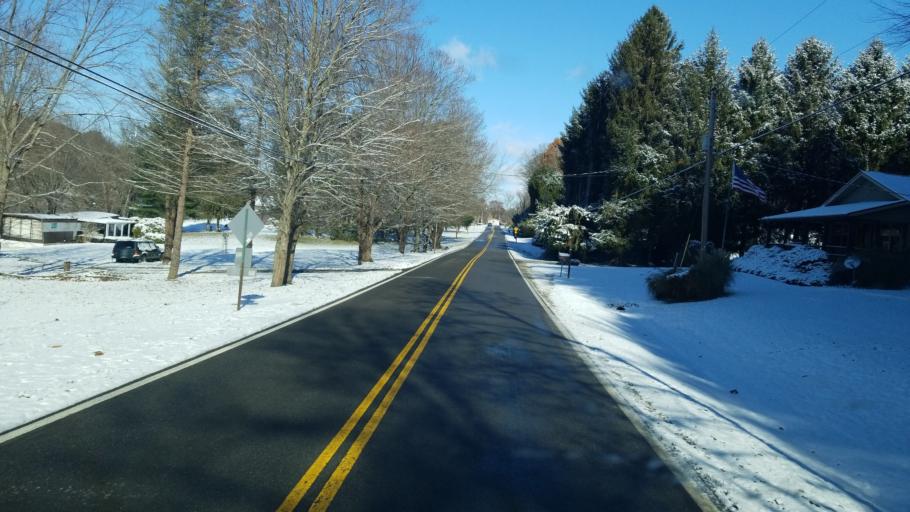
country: US
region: Ohio
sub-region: Licking County
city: Newark
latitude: 40.1472
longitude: -82.3404
